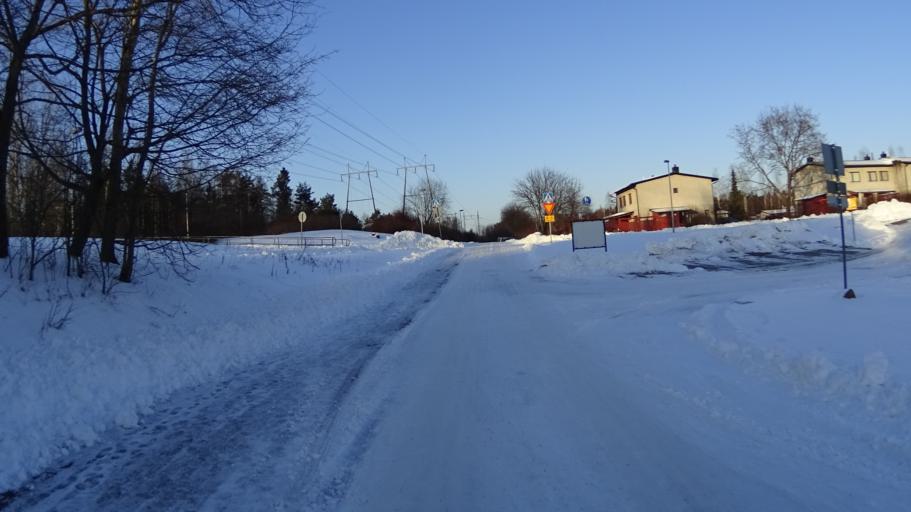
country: FI
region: Uusimaa
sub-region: Helsinki
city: Vantaa
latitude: 60.2490
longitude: 25.1134
